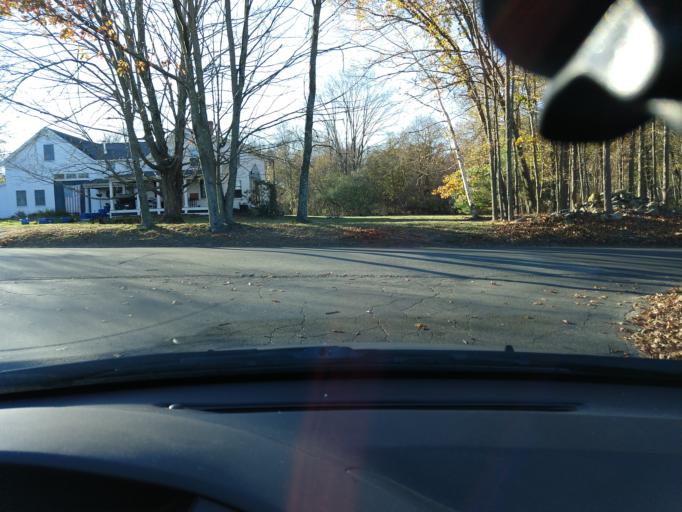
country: US
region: Massachusetts
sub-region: Middlesex County
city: Carlisle
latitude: 42.5022
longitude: -71.3312
